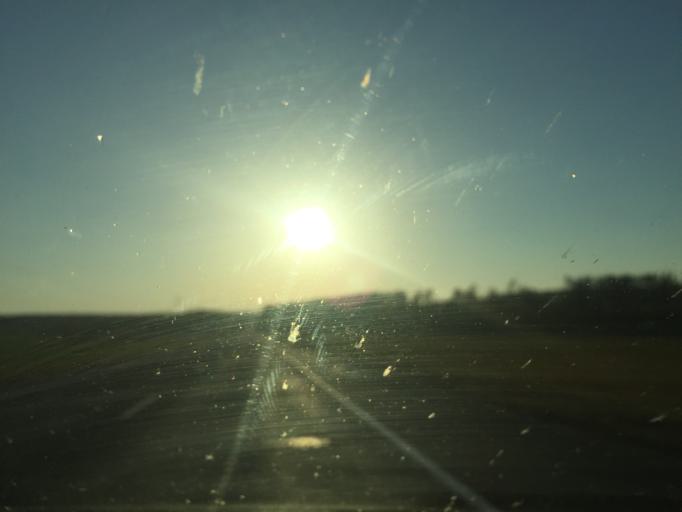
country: BY
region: Mogilev
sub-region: Mahilyowski Rayon
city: Veyno
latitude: 53.7828
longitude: 30.4067
